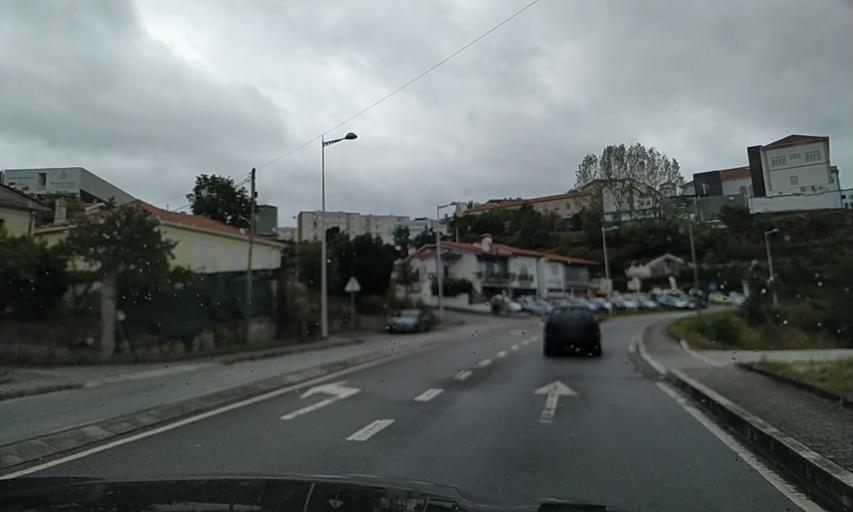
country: PT
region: Porto
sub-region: Penafiel
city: Penafiel
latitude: 41.2109
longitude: -8.2843
